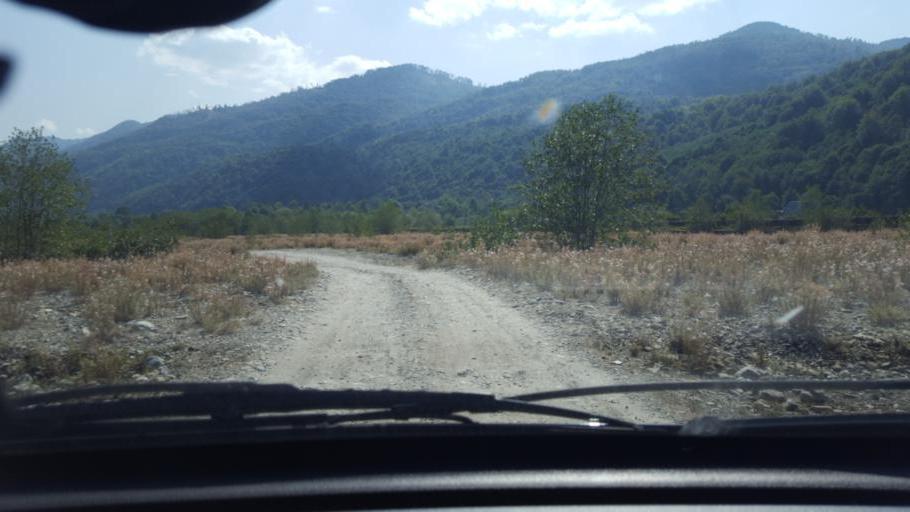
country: ME
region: Andrijevica
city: Andrijevica
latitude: 42.5958
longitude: 19.6736
